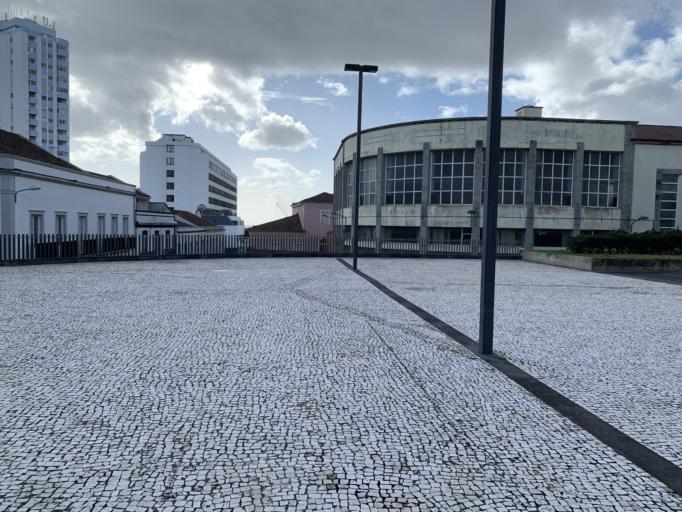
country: PT
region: Azores
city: Ponta Delgada
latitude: 37.7418
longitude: -25.6657
